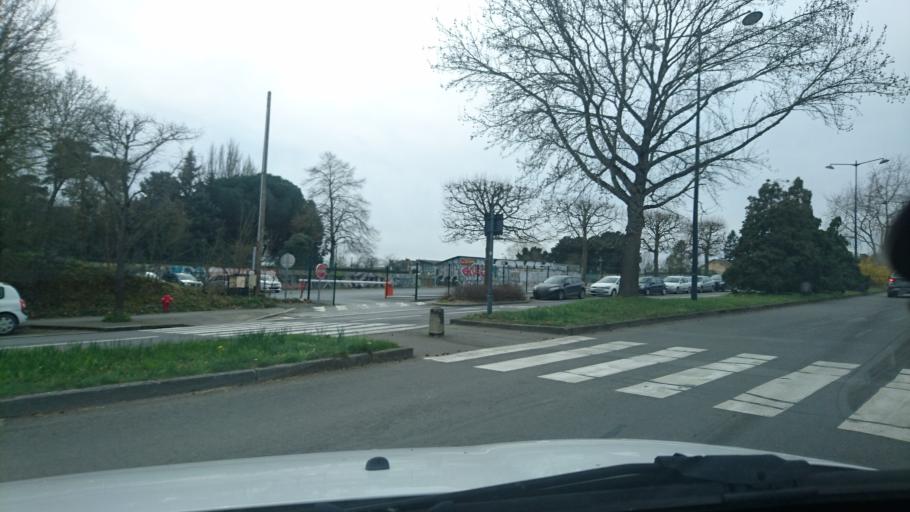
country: FR
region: Brittany
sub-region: Departement d'Ille-et-Vilaine
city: Rennes
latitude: 48.1141
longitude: -1.6983
